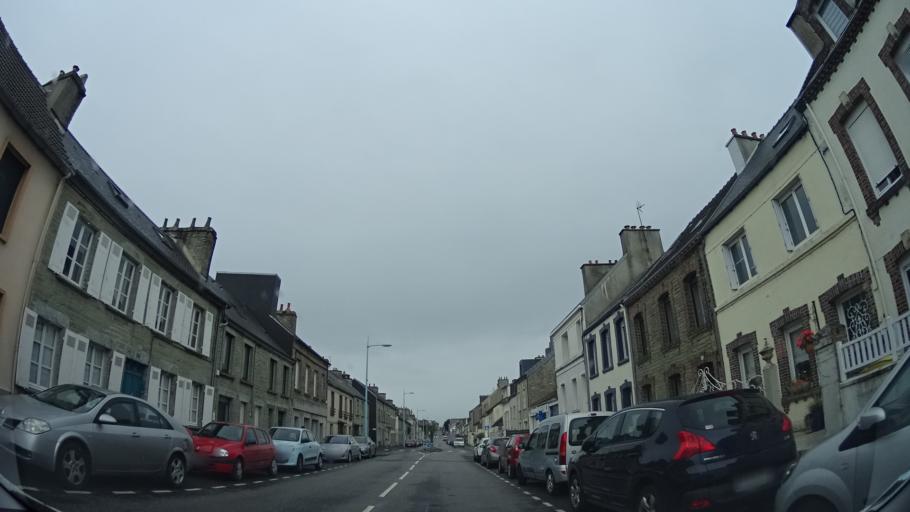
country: FR
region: Lower Normandy
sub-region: Departement de la Manche
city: Octeville
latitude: 49.6312
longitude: -1.6390
